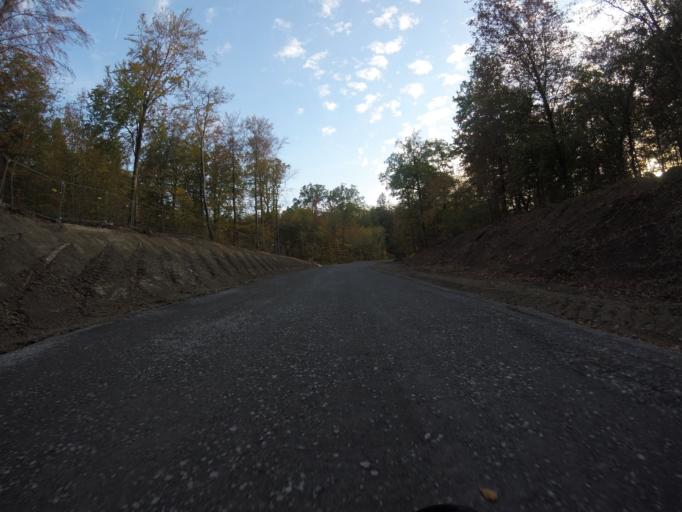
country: DE
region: Baden-Wuerttemberg
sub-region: Regierungsbezirk Stuttgart
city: Kirchberg an der Murr
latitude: 48.9780
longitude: 9.3460
